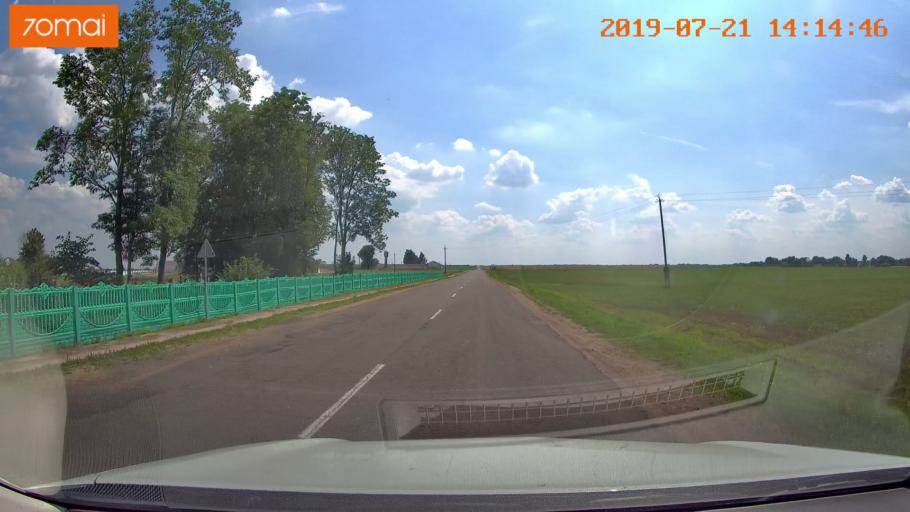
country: BY
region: Grodnenskaya
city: Karelichy
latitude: 53.6439
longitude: 26.1681
